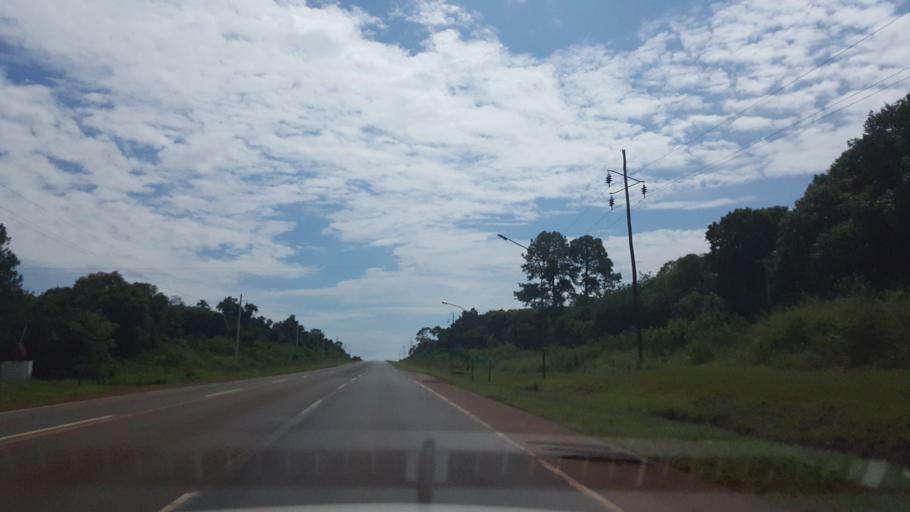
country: AR
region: Misiones
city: Capiovi
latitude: -26.8912
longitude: -55.0558
